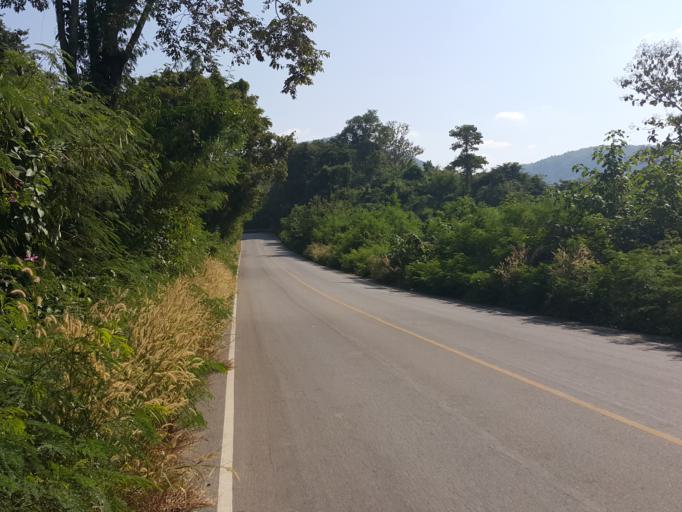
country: TH
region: Sukhothai
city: Thung Saliam
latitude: 17.3376
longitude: 99.4754
